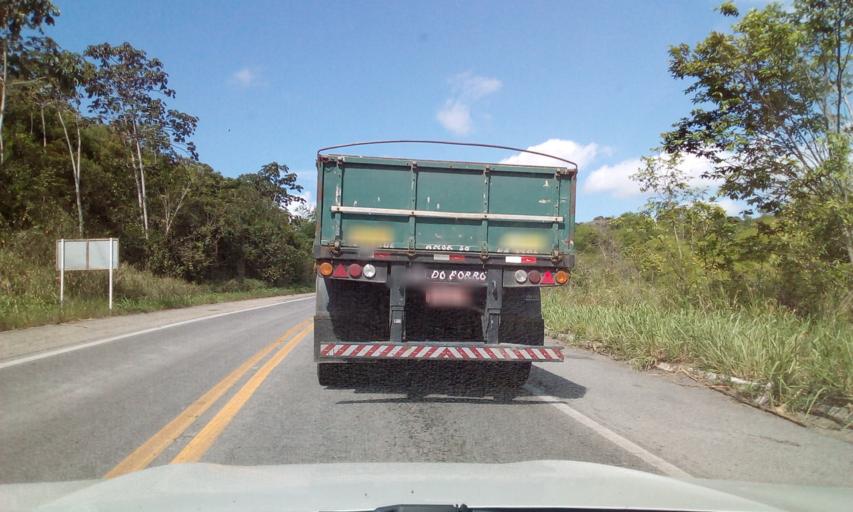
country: BR
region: Alagoas
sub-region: Pilar
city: Pilar
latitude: -9.5230
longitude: -35.9407
